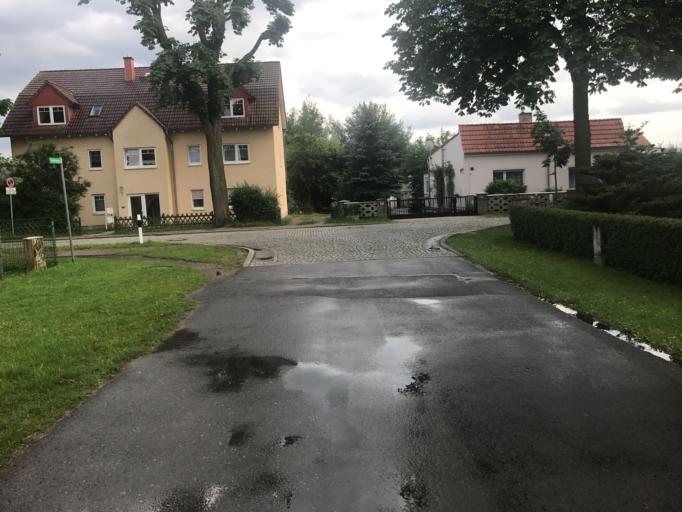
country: DE
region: Brandenburg
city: Melchow
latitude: 52.8482
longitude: 13.6809
